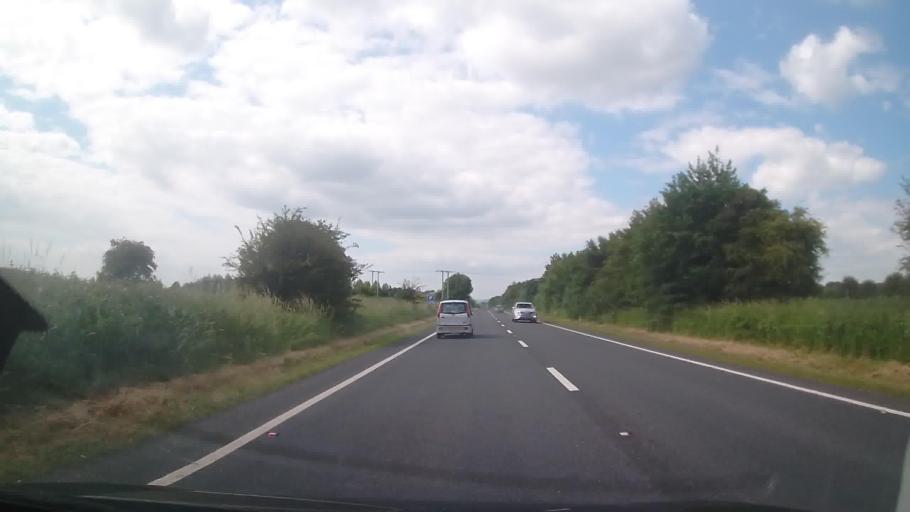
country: GB
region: England
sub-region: Herefordshire
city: Hope under Dinmore
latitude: 52.2042
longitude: -2.7208
